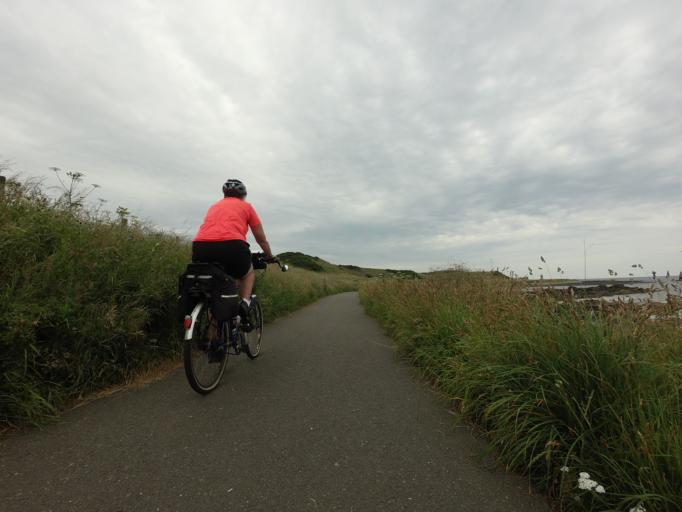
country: GB
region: Scotland
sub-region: Aberdeenshire
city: Whitehills
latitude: 57.6747
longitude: -2.5668
